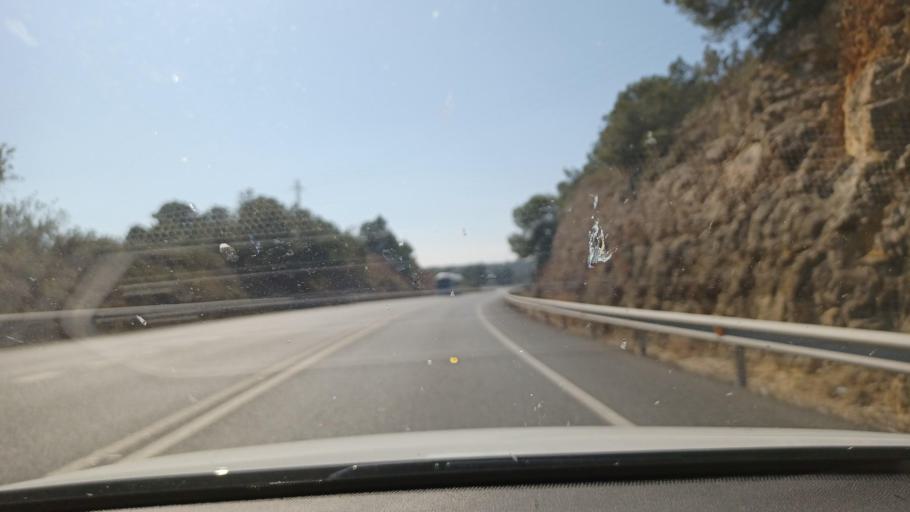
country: ES
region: Catalonia
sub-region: Provincia de Tarragona
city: El Perello
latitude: 40.8481
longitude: 0.7121
